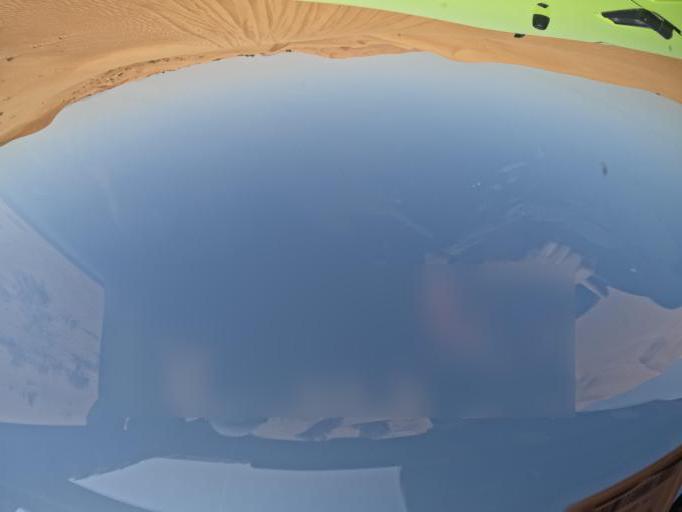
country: AE
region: Ash Shariqah
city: Adh Dhayd
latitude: 24.9645
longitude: 55.7201
